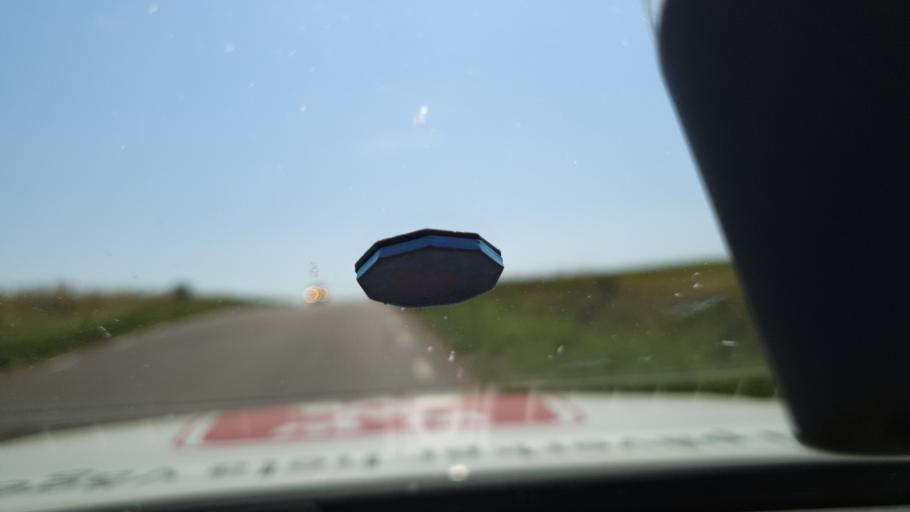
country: SE
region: Skane
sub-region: Sjobo Kommun
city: Blentarp
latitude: 55.5585
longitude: 13.5614
